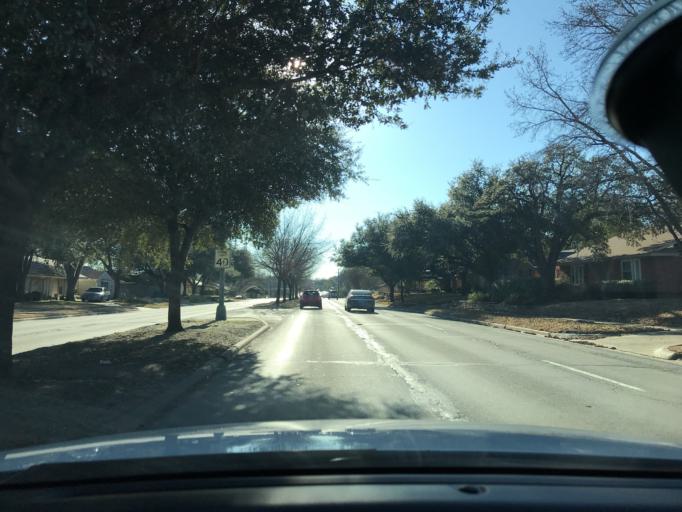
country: US
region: Texas
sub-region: Dallas County
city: Highland Park
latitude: 32.8411
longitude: -96.7433
